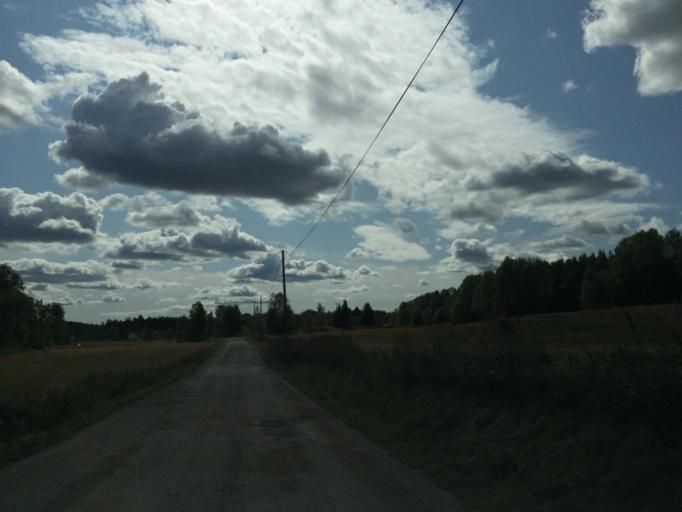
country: NO
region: Ostfold
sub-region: Hobol
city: Elvestad
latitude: 59.5995
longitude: 10.9221
